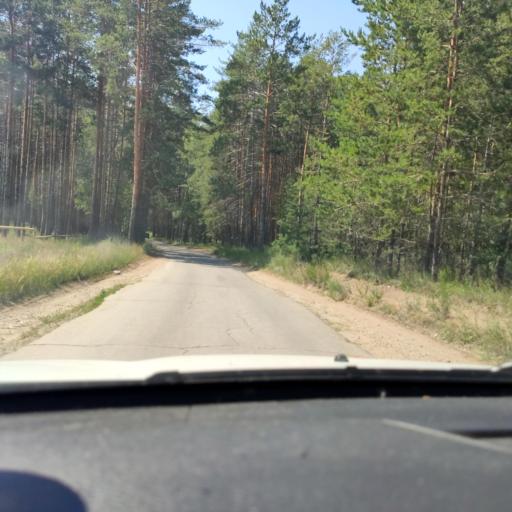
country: RU
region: Samara
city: Pribrezhnyy
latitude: 53.4778
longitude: 49.7974
